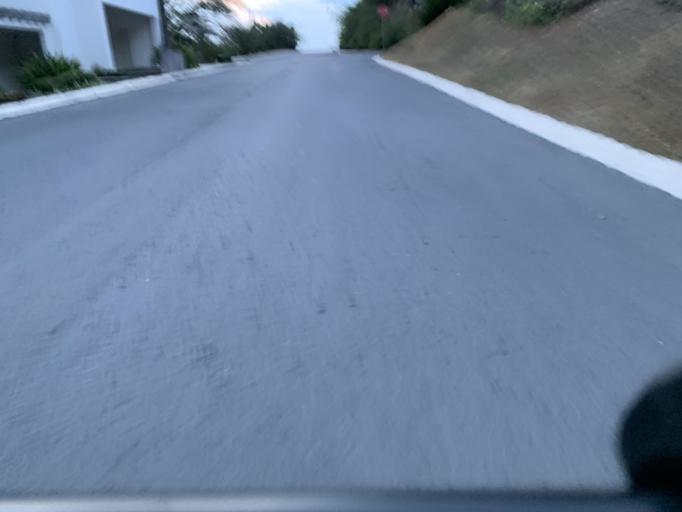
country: MX
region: Nuevo Leon
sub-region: Juarez
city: Bosques de San Pedro
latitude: 25.5169
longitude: -100.1851
